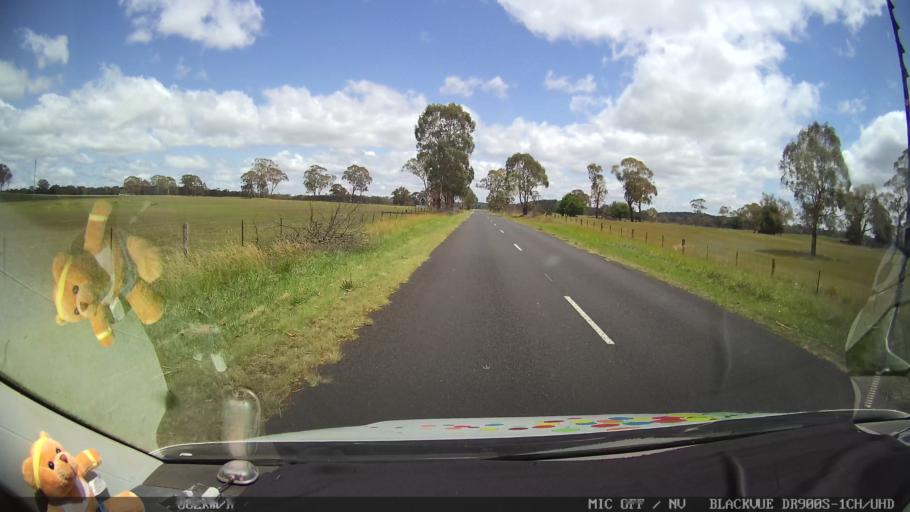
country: AU
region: New South Wales
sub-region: Glen Innes Severn
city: Glen Innes
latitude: -29.6228
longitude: 151.6700
